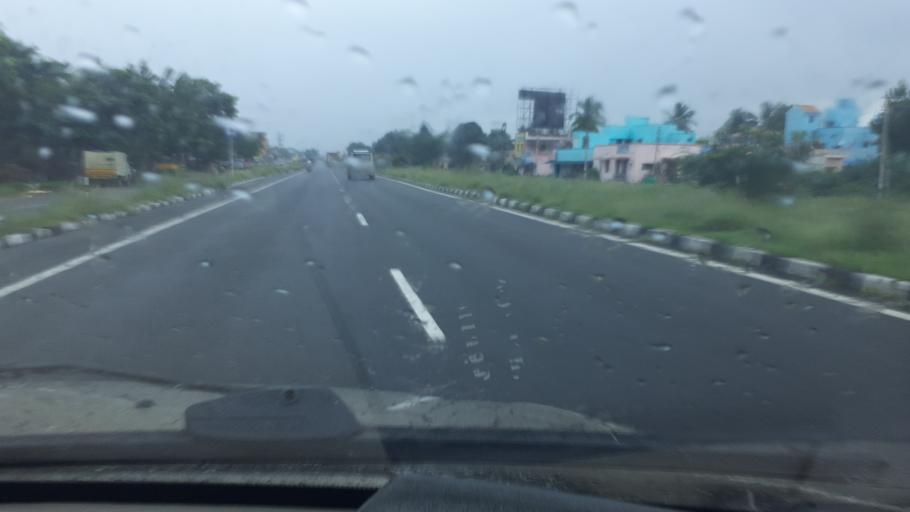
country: IN
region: Tamil Nadu
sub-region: Virudhunagar
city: Virudunagar
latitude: 9.6154
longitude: 77.9572
